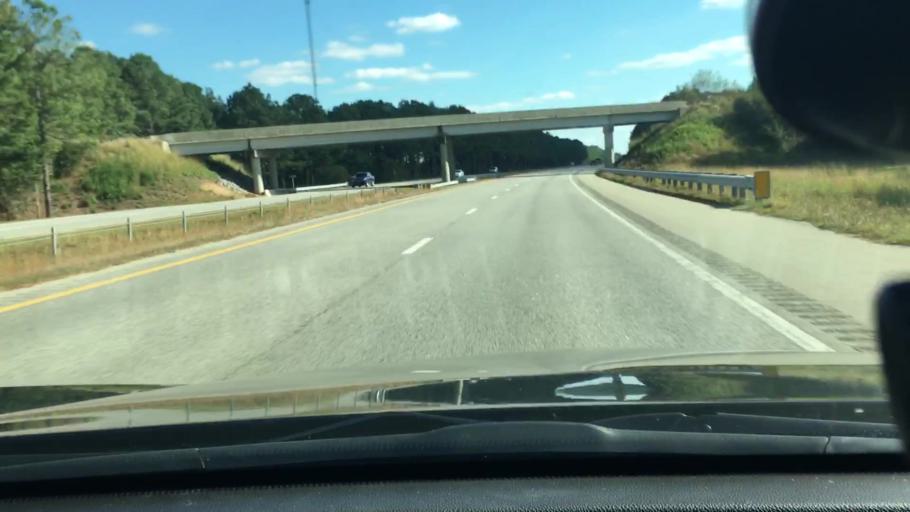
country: US
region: North Carolina
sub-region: Pitt County
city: Farmville
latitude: 35.6554
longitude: -77.7446
